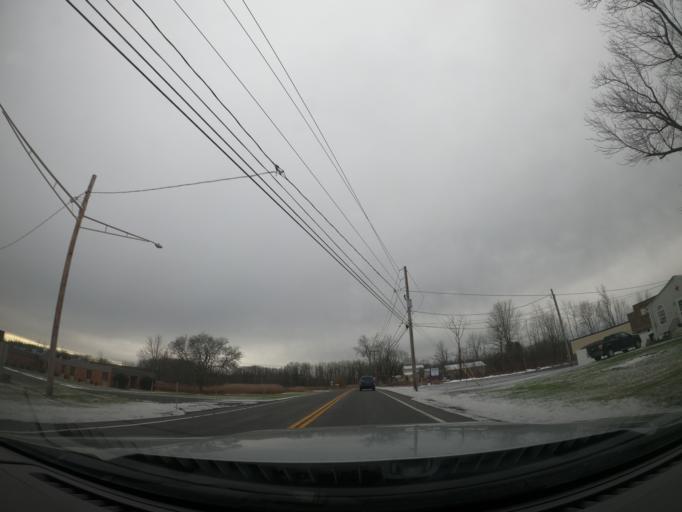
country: US
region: New York
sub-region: Onondaga County
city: Minoa
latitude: 43.1091
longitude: -76.0386
